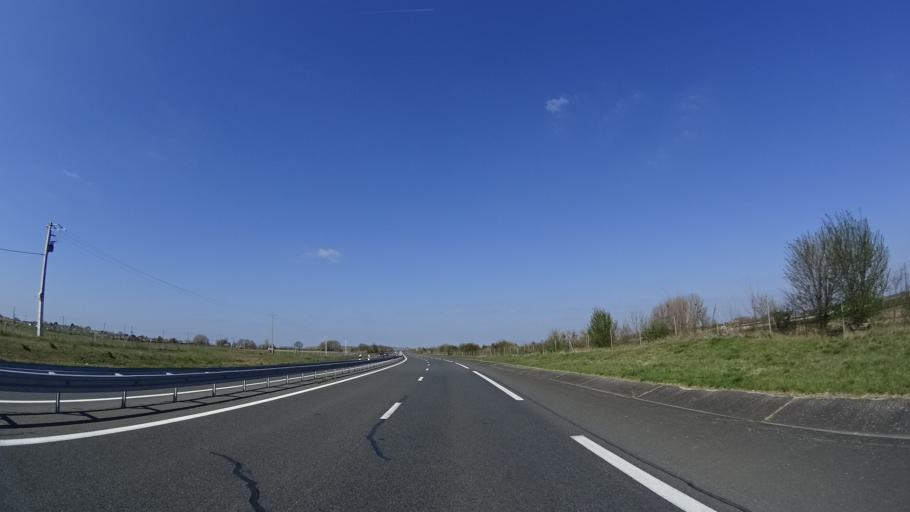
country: FR
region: Pays de la Loire
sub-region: Departement de Maine-et-Loire
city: Saint-Jean
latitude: 47.2742
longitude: -0.3385
